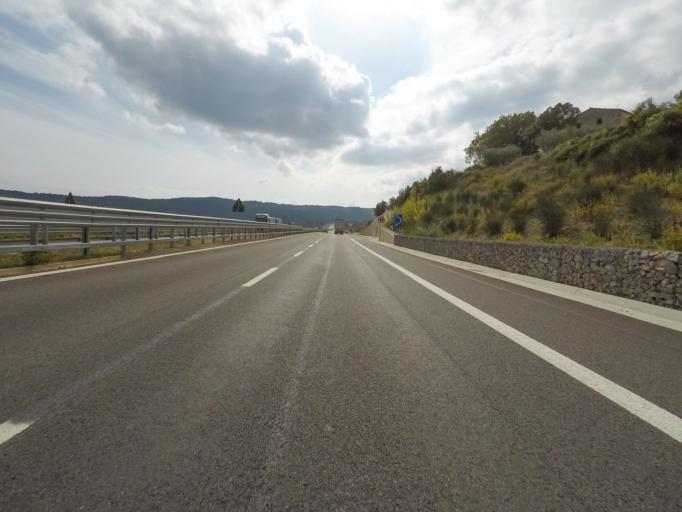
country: IT
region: Tuscany
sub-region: Provincia di Grosseto
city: Civitella Marittima
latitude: 43.0838
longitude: 11.2944
